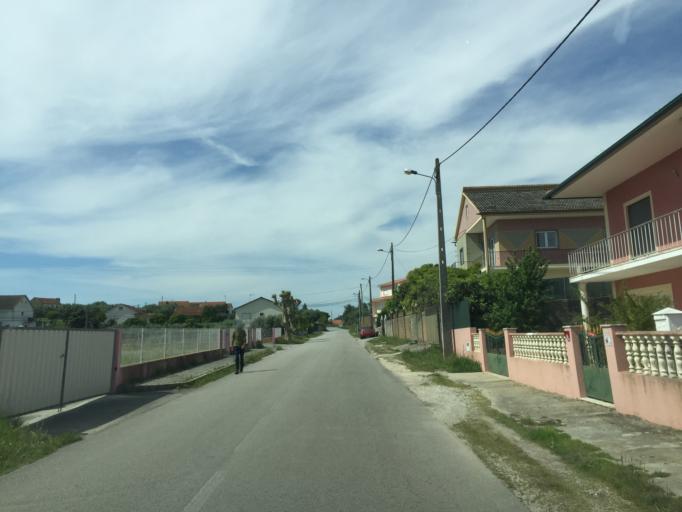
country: PT
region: Coimbra
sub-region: Soure
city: Soure
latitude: 40.0121
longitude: -8.5804
